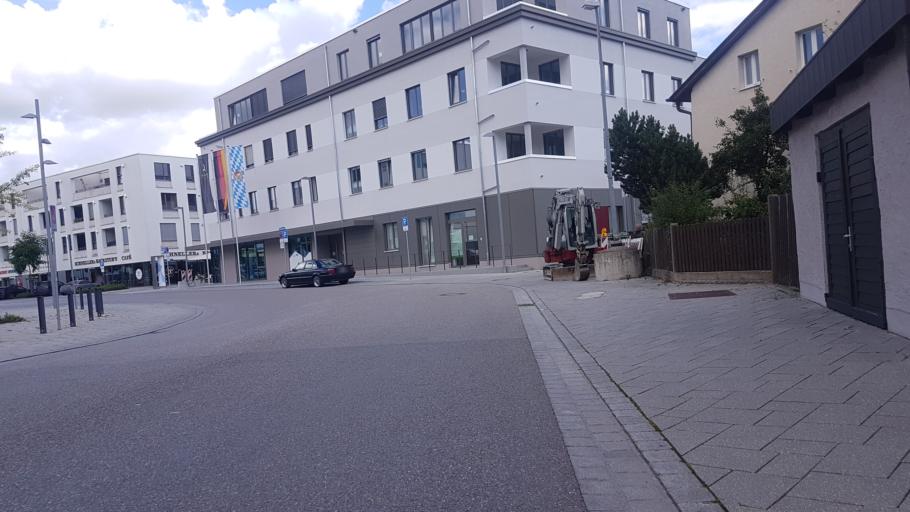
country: DE
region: Bavaria
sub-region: Upper Bavaria
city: Eichstaett
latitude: 48.8927
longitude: 11.1807
